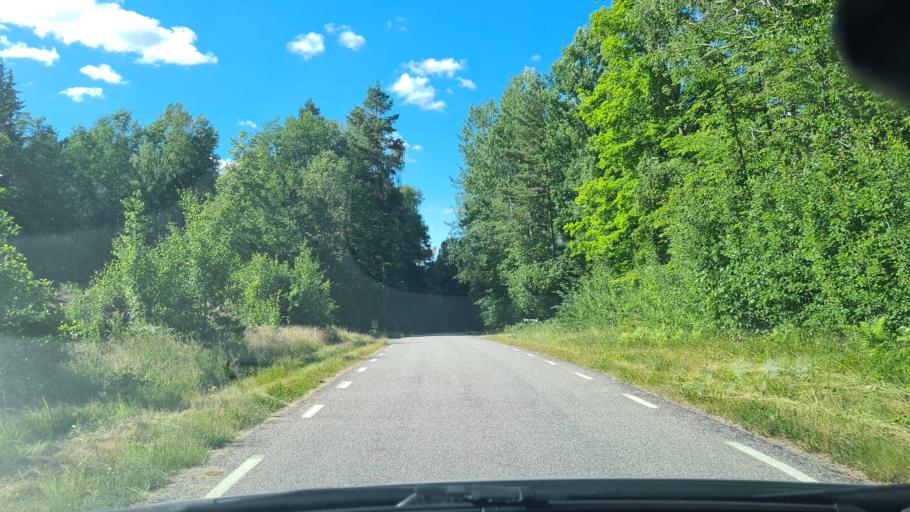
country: SE
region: OEstergoetland
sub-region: Norrkopings Kommun
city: Krokek
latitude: 58.7231
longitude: 16.4300
